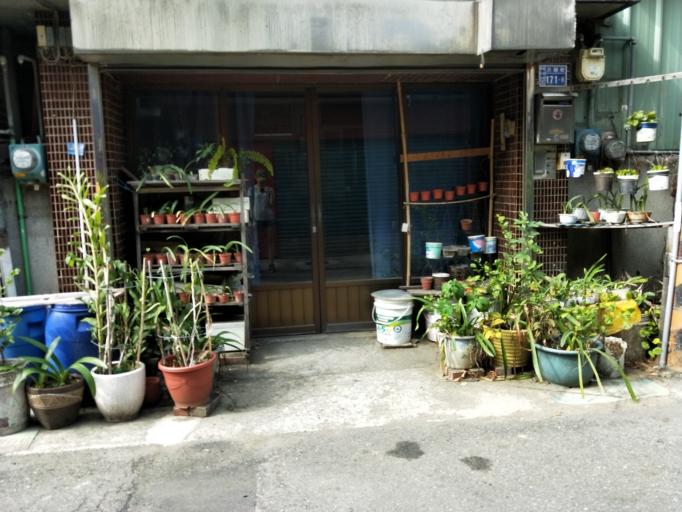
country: TW
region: Taiwan
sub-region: Changhua
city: Chang-hua
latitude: 24.0889
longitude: 120.5489
